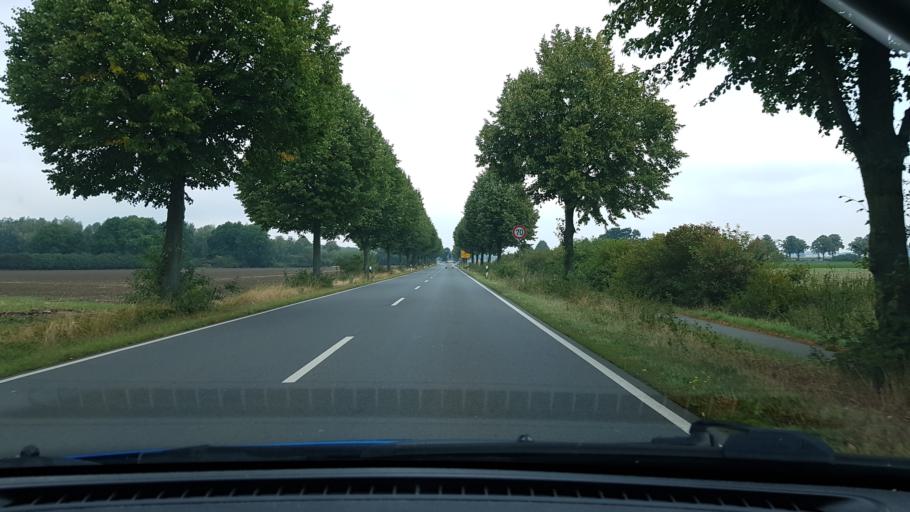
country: DE
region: Lower Saxony
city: Grossgoltern
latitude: 52.3292
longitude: 9.4691
